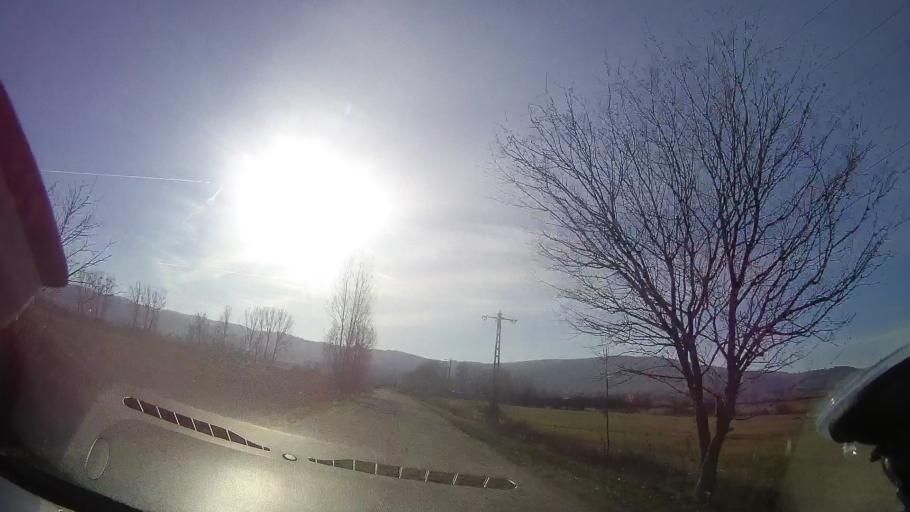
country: RO
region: Bihor
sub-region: Comuna Magesti
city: Magesti
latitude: 47.0148
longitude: 22.4579
